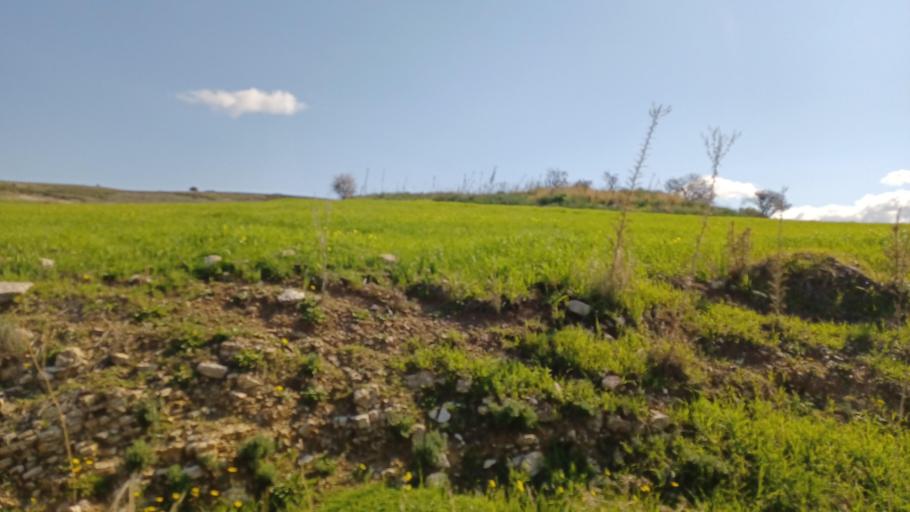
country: CY
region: Pafos
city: Mesogi
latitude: 34.7552
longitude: 32.5337
